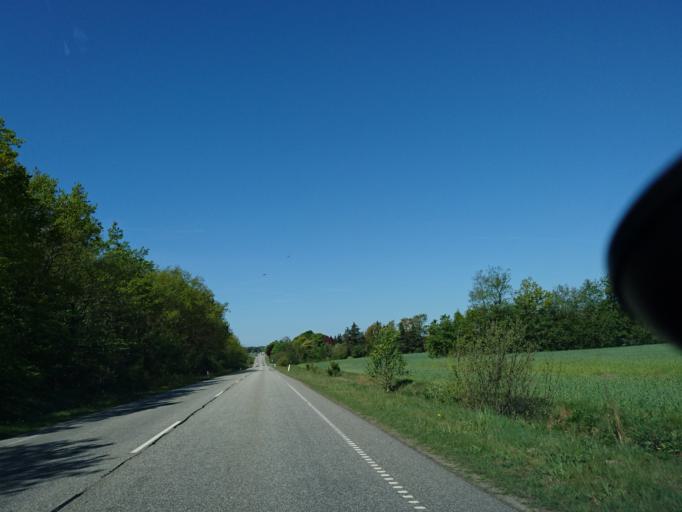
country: DK
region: North Denmark
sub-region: Hjorring Kommune
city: Sindal
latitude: 57.4660
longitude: 10.2692
